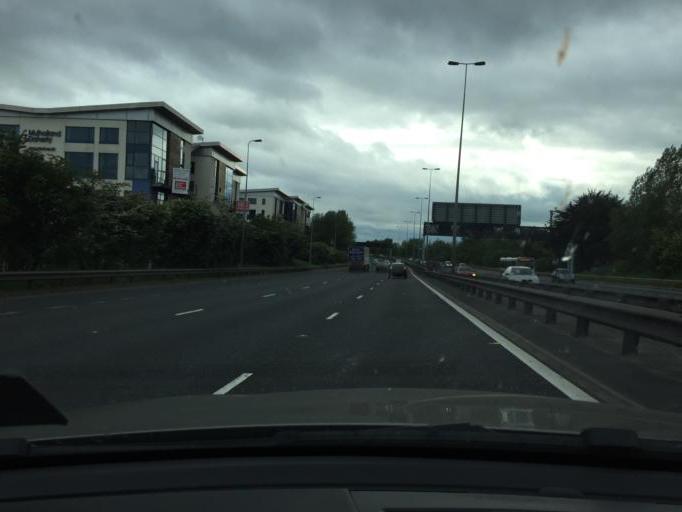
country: GB
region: Northern Ireland
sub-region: City of Belfast
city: Belfast
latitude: 54.5714
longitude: -5.9830
